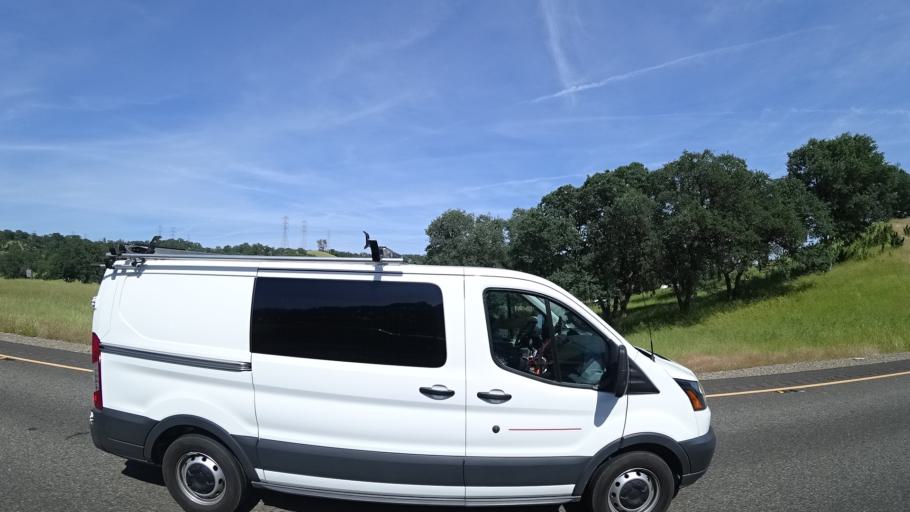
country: US
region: California
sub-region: Tehama County
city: Red Bluff
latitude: 40.2749
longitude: -122.2713
